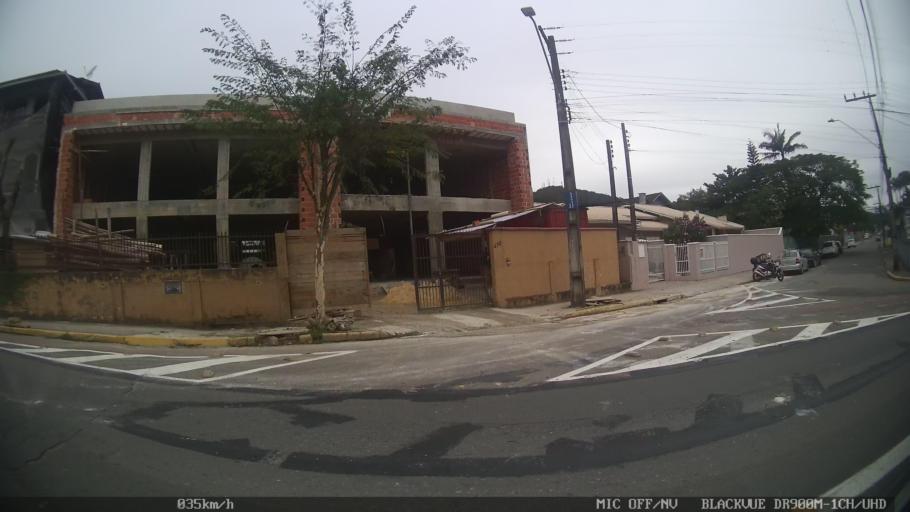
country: BR
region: Santa Catarina
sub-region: Joinville
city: Joinville
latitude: -26.2817
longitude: -48.8345
